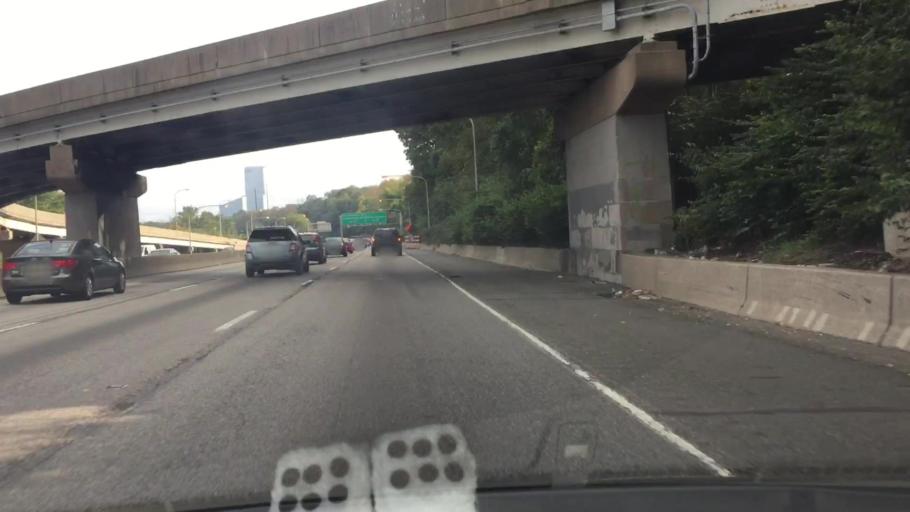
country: US
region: Pennsylvania
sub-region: Philadelphia County
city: Philadelphia
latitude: 39.9743
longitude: -75.1943
